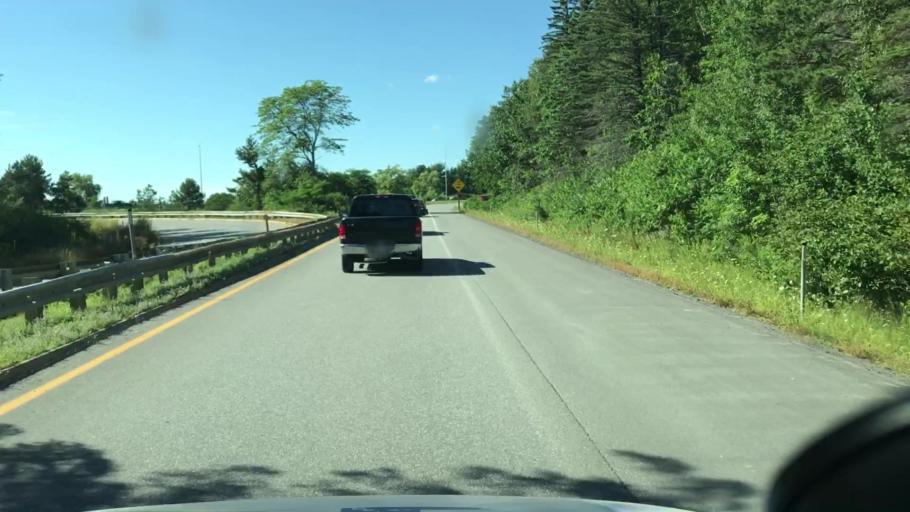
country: US
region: Maine
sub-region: Penobscot County
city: Bangor
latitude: 44.7878
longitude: -68.8052
